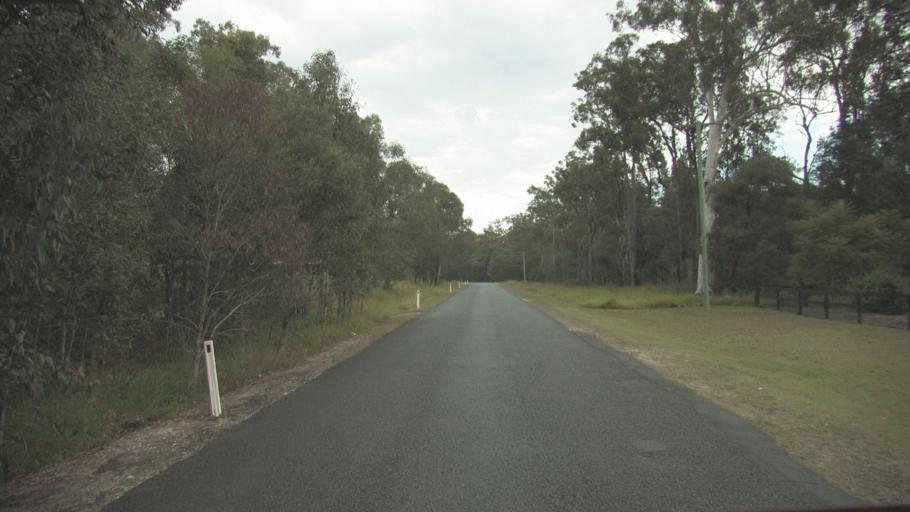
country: AU
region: Queensland
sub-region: Logan
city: Chambers Flat
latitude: -27.7852
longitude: 153.1092
